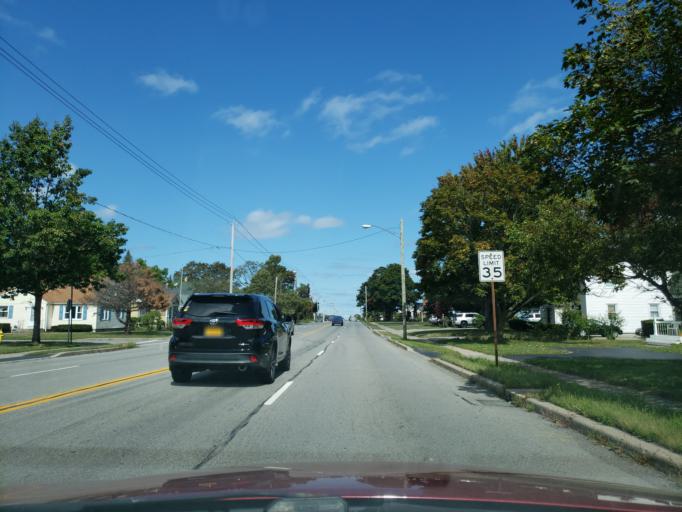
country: US
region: New York
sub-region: Monroe County
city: Greece
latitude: 43.2332
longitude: -77.6469
